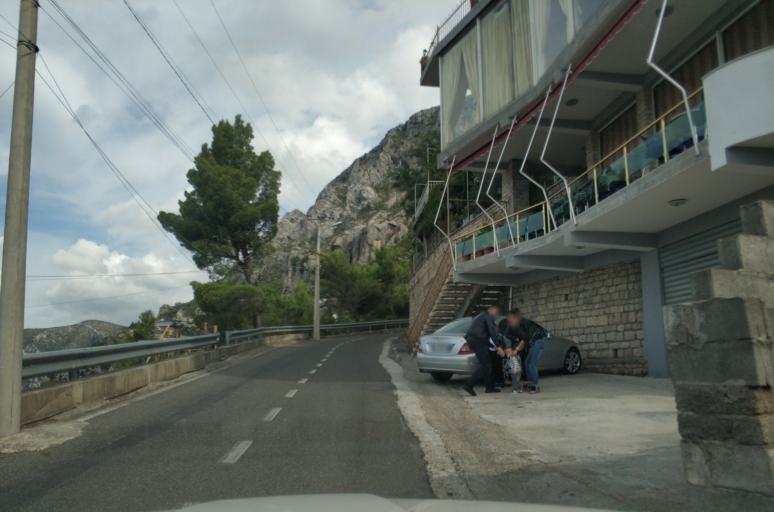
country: AL
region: Durres
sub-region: Rrethi i Krujes
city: Kruje
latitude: 41.5163
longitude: 19.7937
